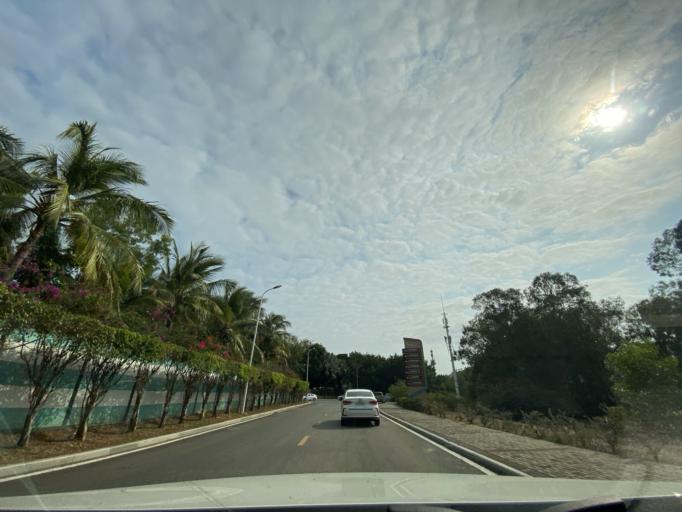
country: CN
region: Hainan
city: Tiandu
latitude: 18.2282
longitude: 109.6217
